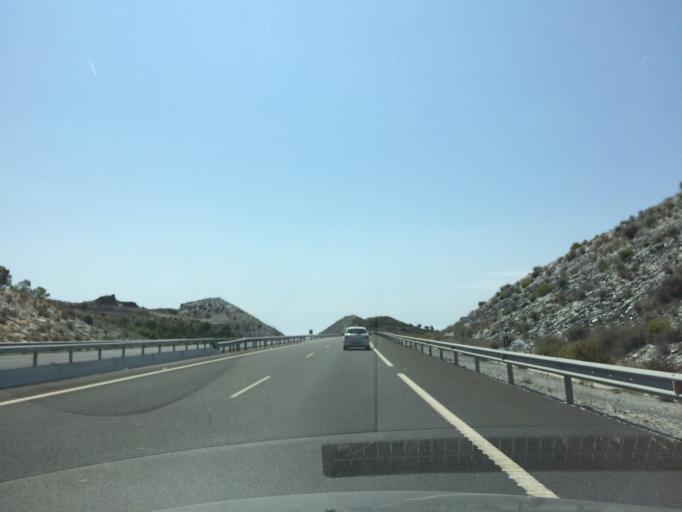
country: ES
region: Andalusia
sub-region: Provincia de Granada
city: Motril
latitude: 36.7654
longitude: -3.4851
